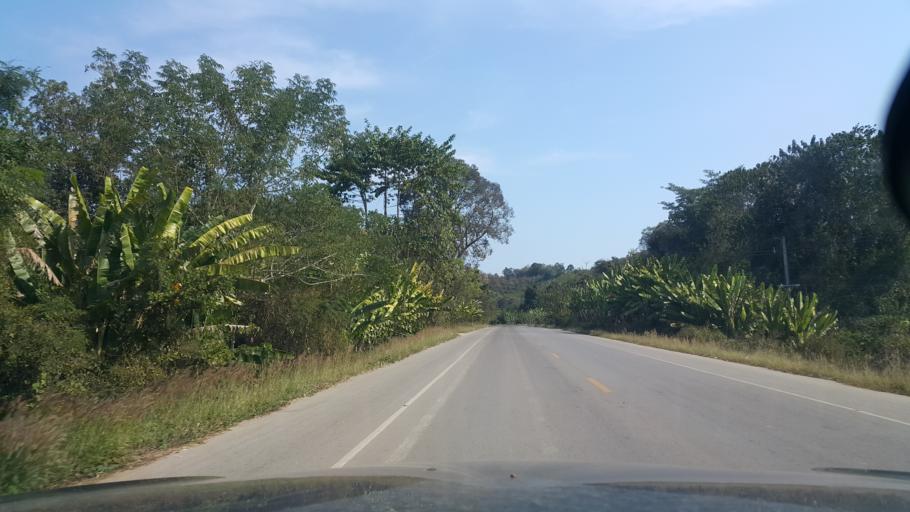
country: TH
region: Loei
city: Pak Chom
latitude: 18.0915
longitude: 101.9580
